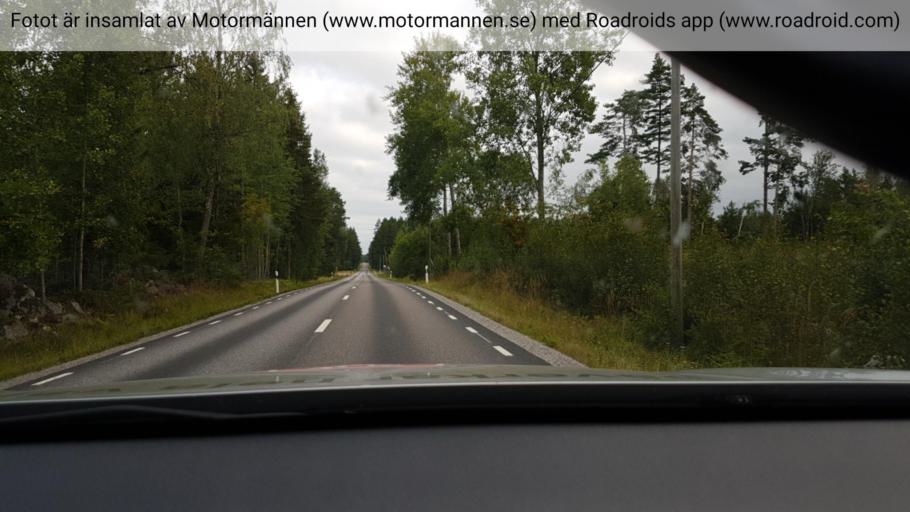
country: SE
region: Stockholm
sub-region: Norrtalje Kommun
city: Rimbo
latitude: 59.8069
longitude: 18.4410
